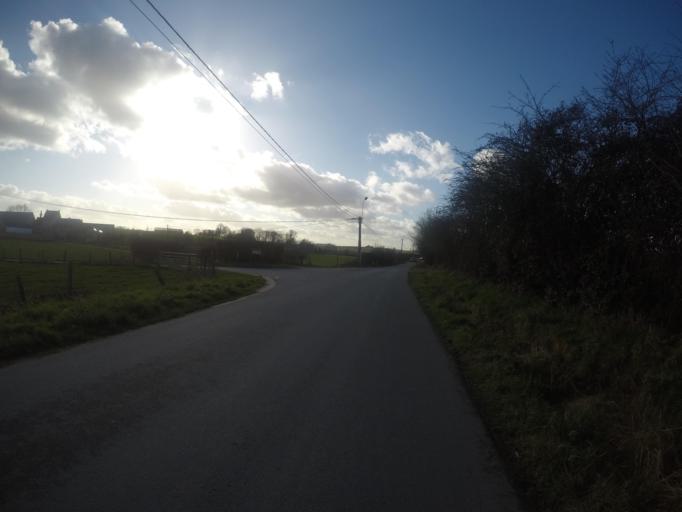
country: BE
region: Wallonia
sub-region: Province du Brabant Wallon
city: Tubize
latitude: 50.6993
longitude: 4.1539
